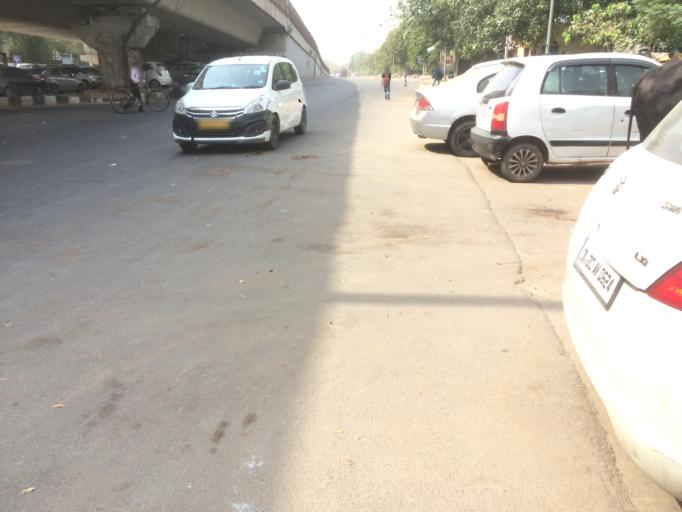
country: IN
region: NCT
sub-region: Central Delhi
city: Karol Bagh
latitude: 28.6191
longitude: 77.1362
